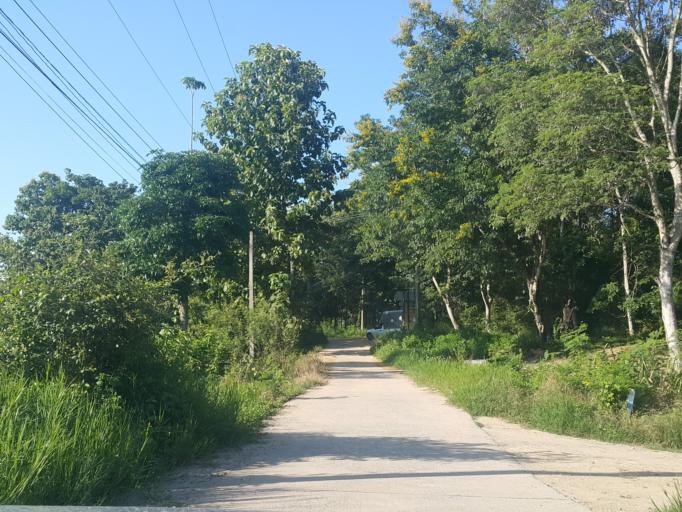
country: TH
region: Chiang Mai
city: Mae On
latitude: 18.7103
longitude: 99.2022
